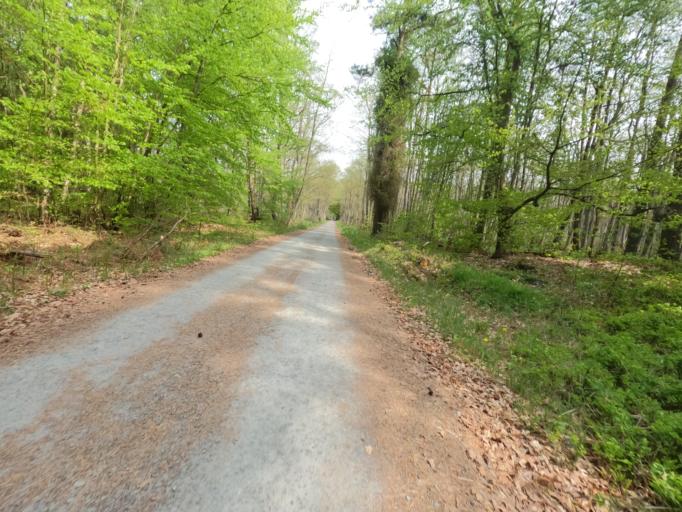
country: DE
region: Mecklenburg-Vorpommern
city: Ostseebad Prerow
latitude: 54.4563
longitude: 12.5129
